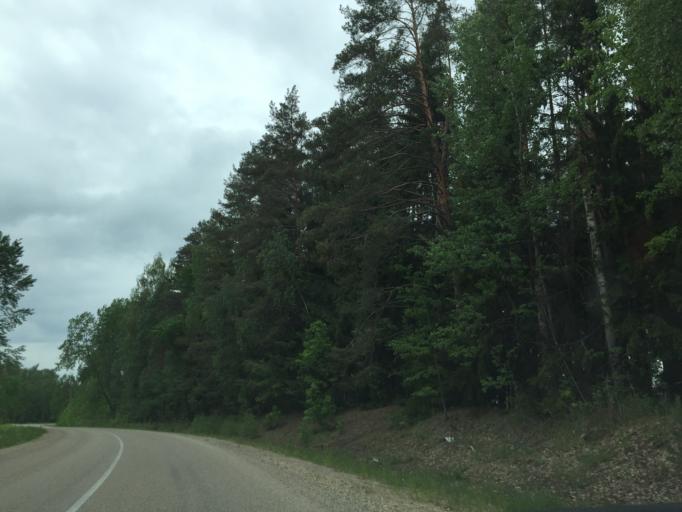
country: LV
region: Varkava
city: Vecvarkava
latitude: 56.0774
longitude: 26.6246
